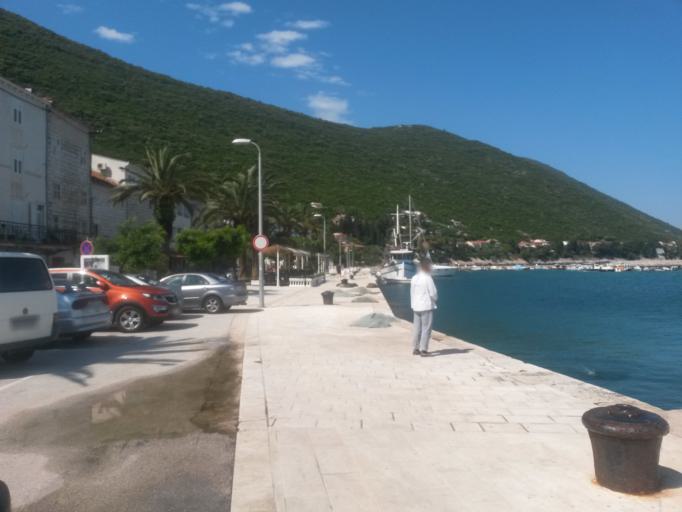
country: HR
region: Dubrovacko-Neretvanska
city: Orebic
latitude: 43.0095
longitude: 17.2677
